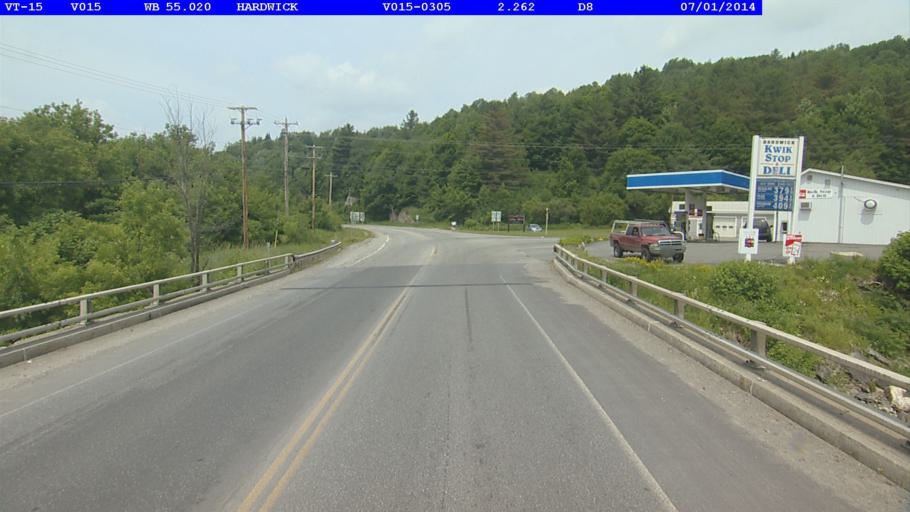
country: US
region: Vermont
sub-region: Caledonia County
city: Hardwick
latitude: 44.5168
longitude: -72.3784
